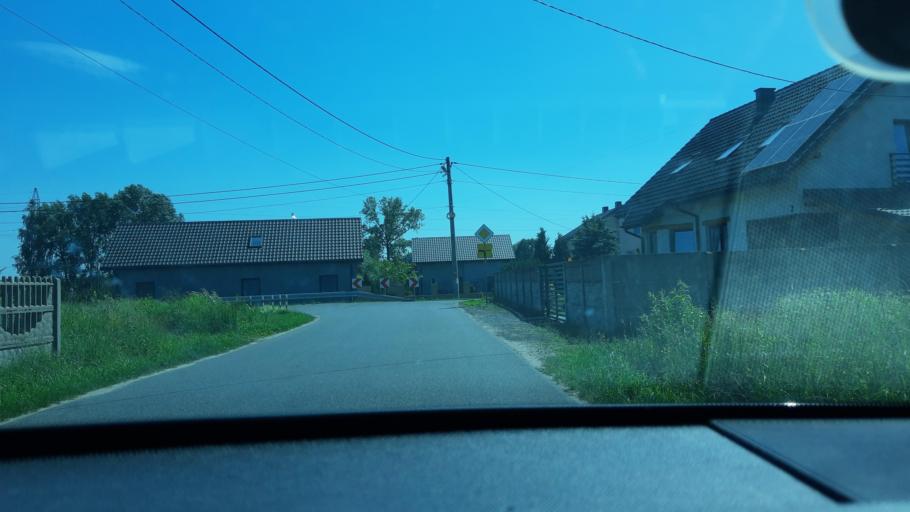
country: PL
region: Lodz Voivodeship
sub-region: Powiat zdunskowolski
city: Zdunska Wola
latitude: 51.6183
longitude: 18.9776
